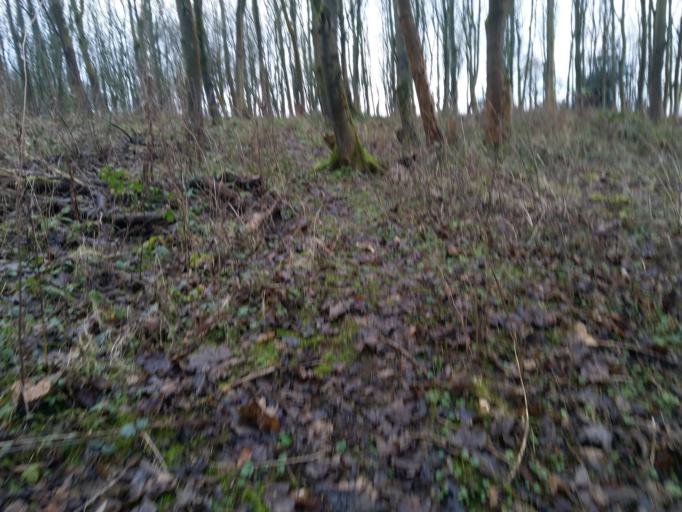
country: GB
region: Scotland
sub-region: Fife
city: Limekilns
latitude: 55.9928
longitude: -3.5154
